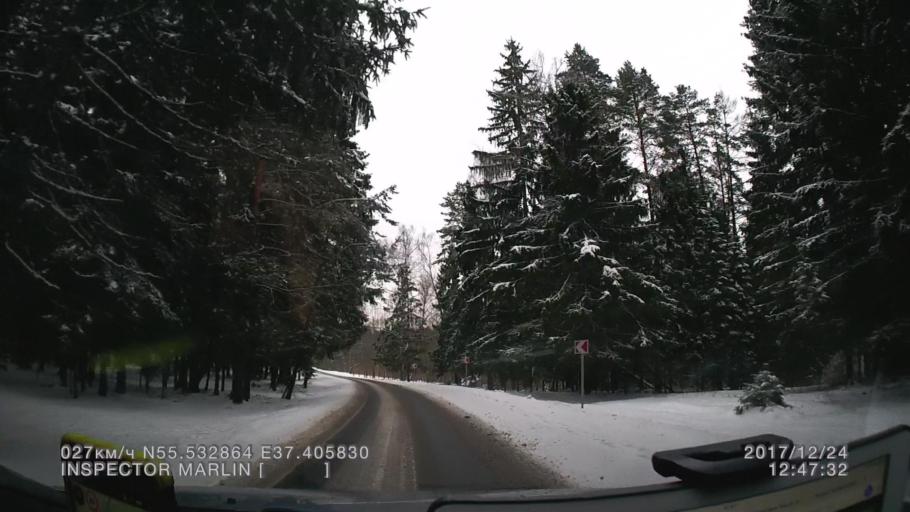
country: RU
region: Moskovskaya
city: Filimonki
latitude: 55.5328
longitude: 37.4058
